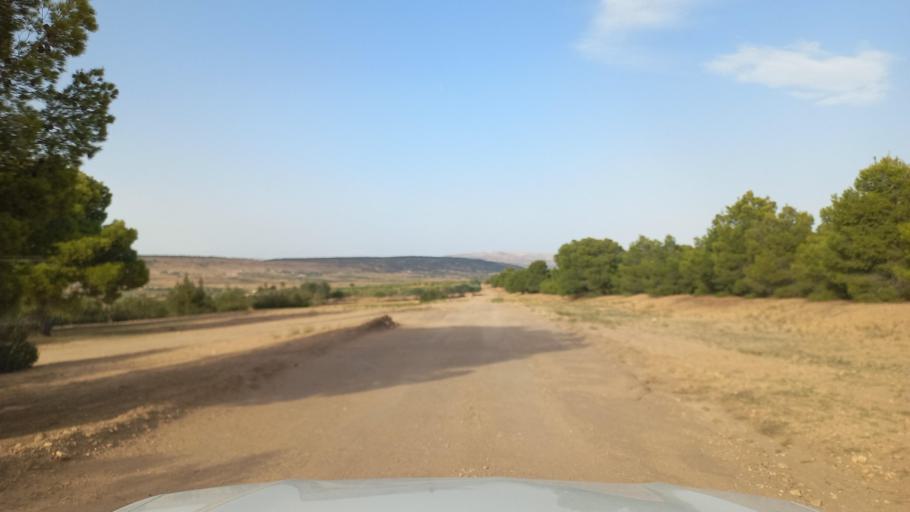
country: TN
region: Al Qasrayn
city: Kasserine
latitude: 35.3437
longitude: 8.8618
